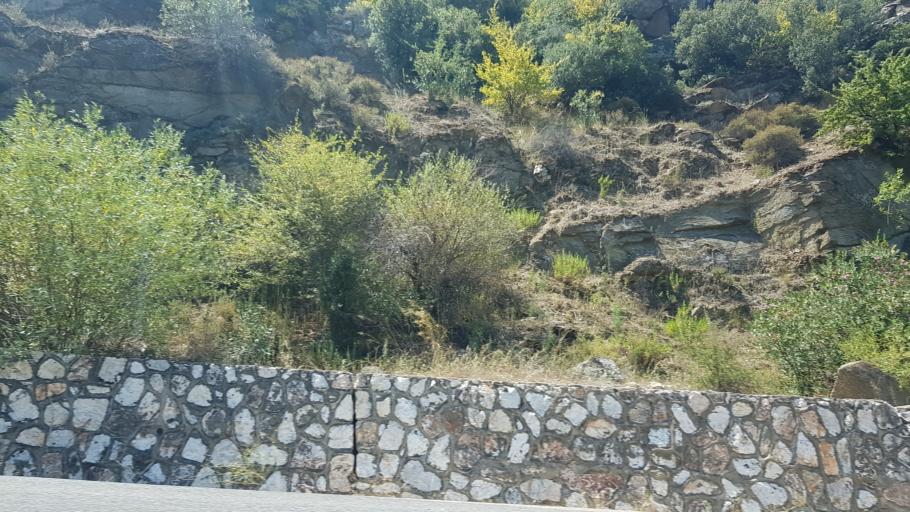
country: TR
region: Aydin
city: Akcaova
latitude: 37.5031
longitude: 28.1036
